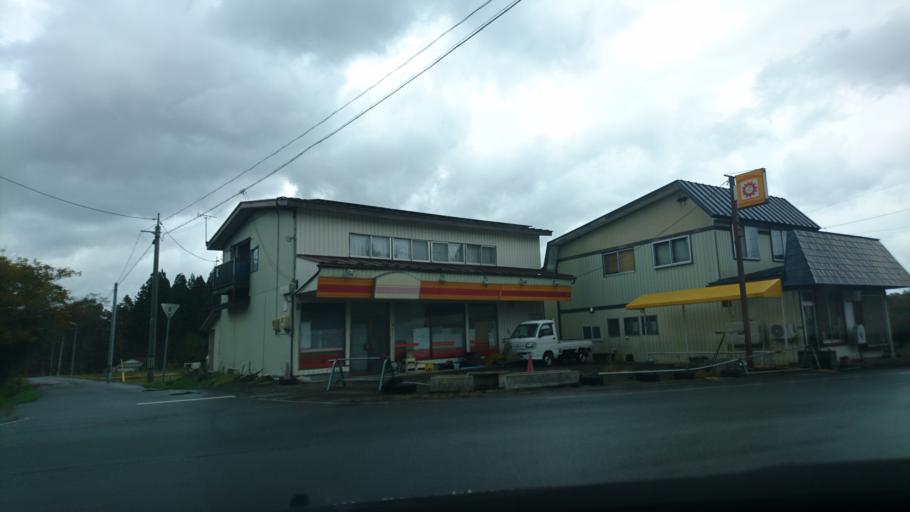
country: JP
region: Iwate
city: Shizukuishi
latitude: 39.6484
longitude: 140.9517
